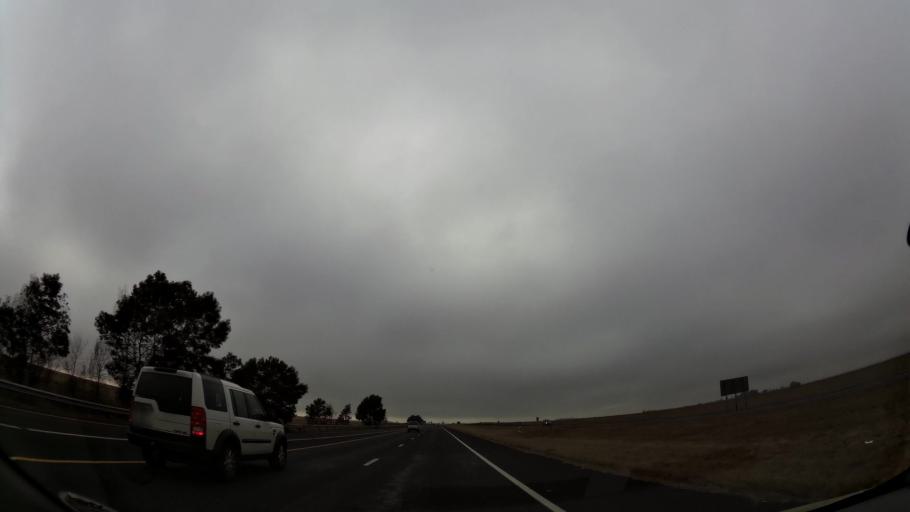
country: ZA
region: Mpumalanga
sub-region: Nkangala District Municipality
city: Delmas
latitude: -26.0697
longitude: 28.7620
